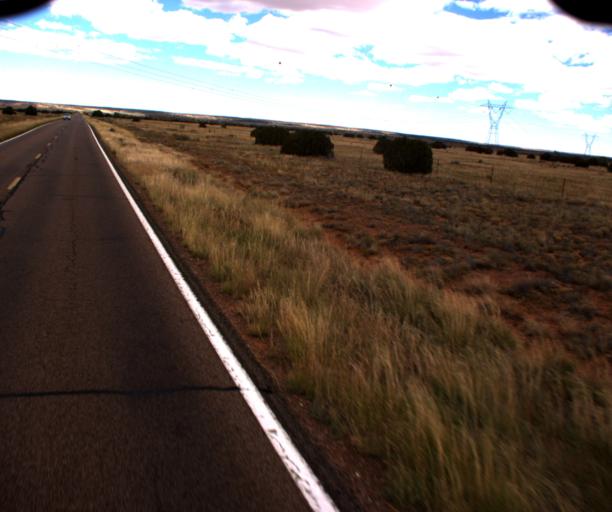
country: US
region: Arizona
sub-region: Navajo County
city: Heber-Overgaard
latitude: 34.5937
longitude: -110.3938
